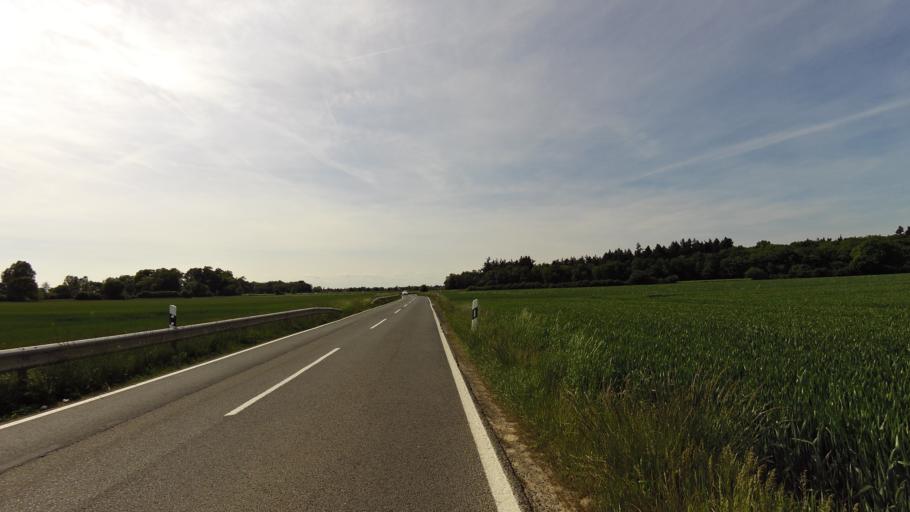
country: DE
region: North Rhine-Westphalia
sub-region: Regierungsbezirk Koln
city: Rheinbach
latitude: 50.6636
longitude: 6.9727
